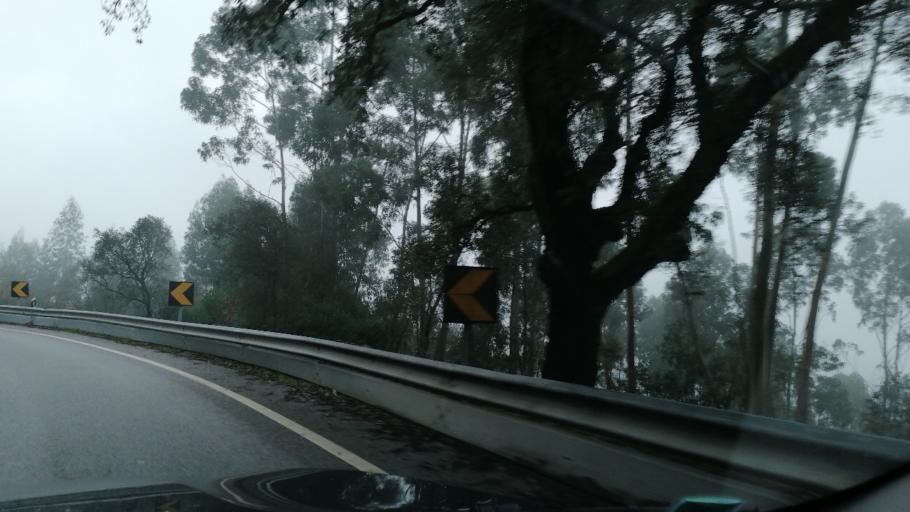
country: PT
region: Aveiro
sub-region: Mealhada
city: Pampilhosa do Botao
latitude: 40.3722
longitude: -8.3503
